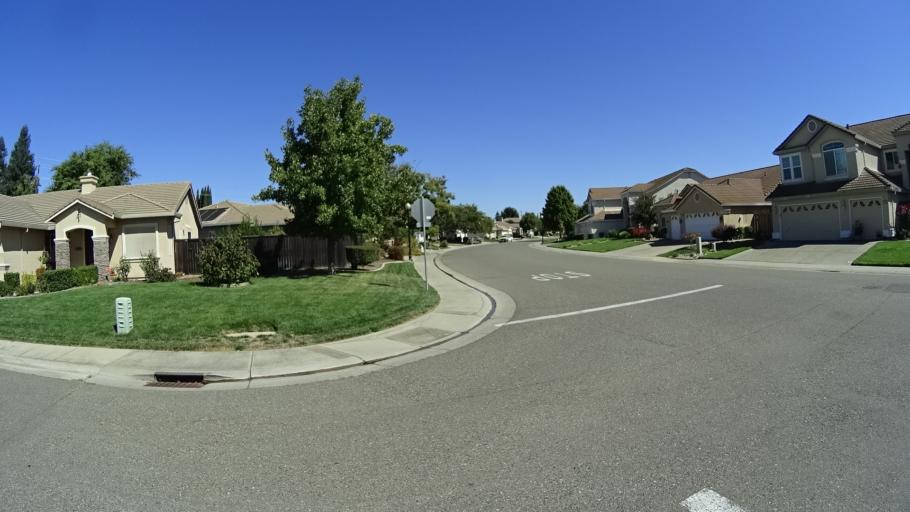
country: US
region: California
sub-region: Sacramento County
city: Laguna
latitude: 38.4154
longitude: -121.4655
